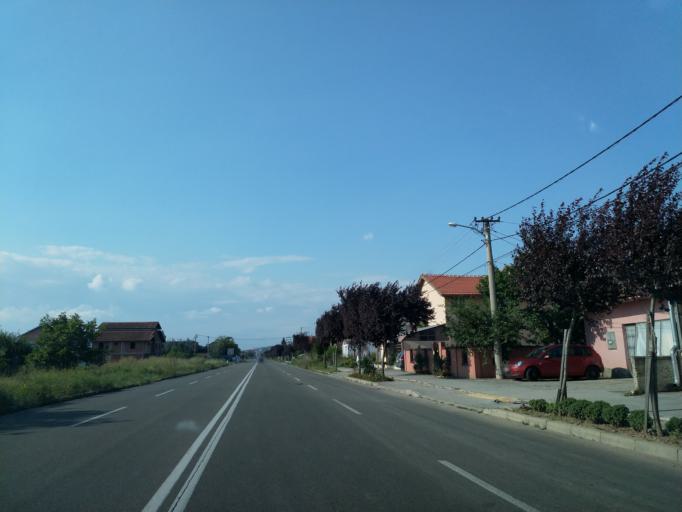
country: RS
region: Central Serbia
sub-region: Pomoravski Okrug
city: Paracin
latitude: 43.8397
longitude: 21.4153
